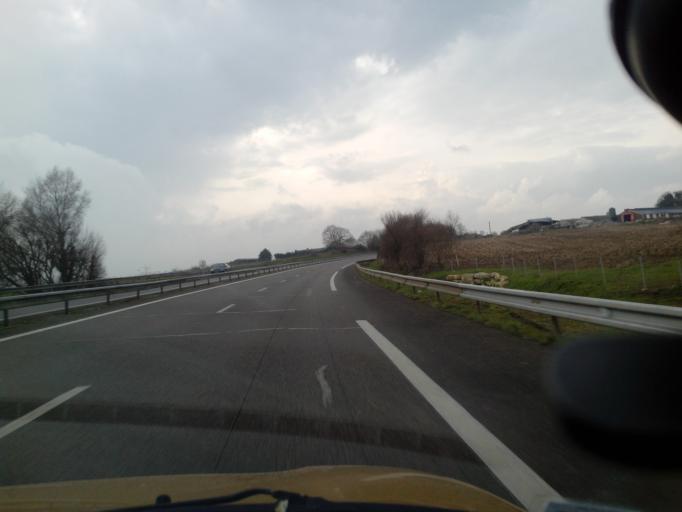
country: FR
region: Brittany
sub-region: Departement du Morbihan
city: Plumelin
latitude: 47.8935
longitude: -2.9254
